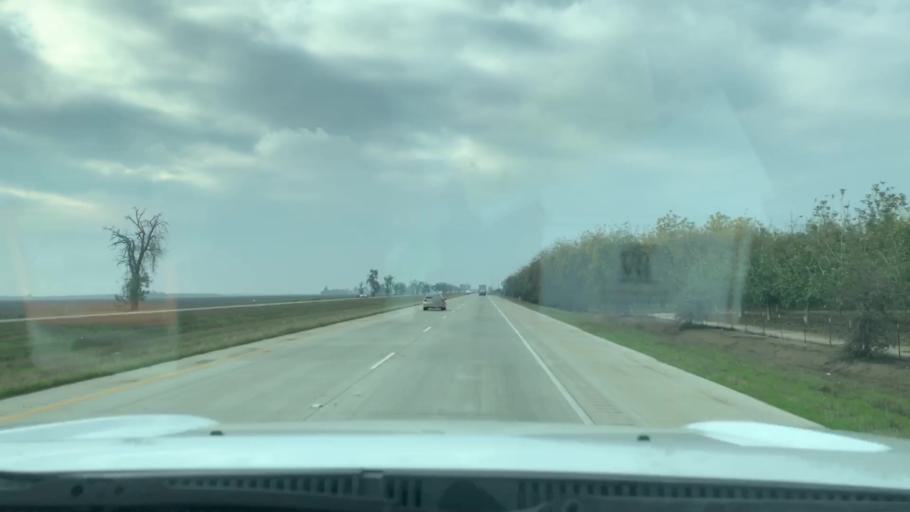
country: US
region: California
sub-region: Tulare County
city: Goshen
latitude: 36.3278
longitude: -119.4521
